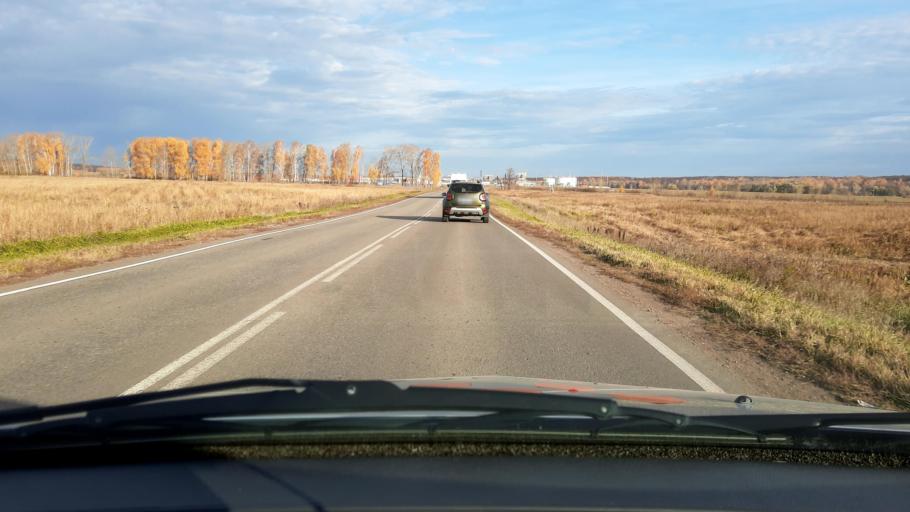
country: RU
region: Bashkortostan
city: Mikhaylovka
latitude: 54.8183
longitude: 55.7674
